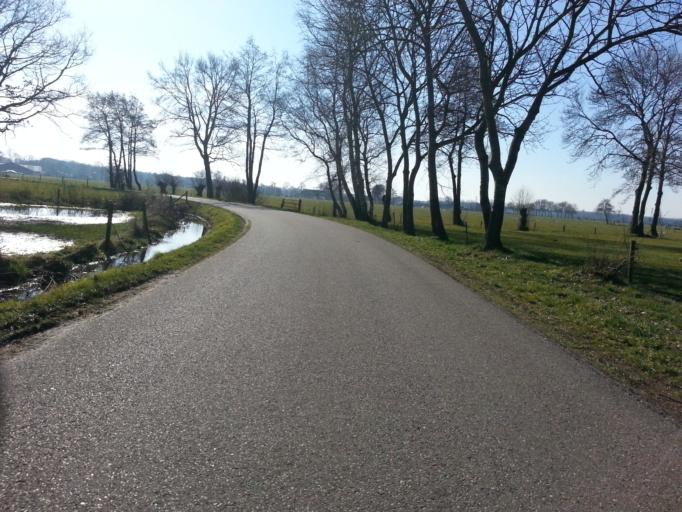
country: NL
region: Utrecht
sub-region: Gemeente Woudenberg
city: Woudenberg
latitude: 52.0721
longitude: 5.4318
